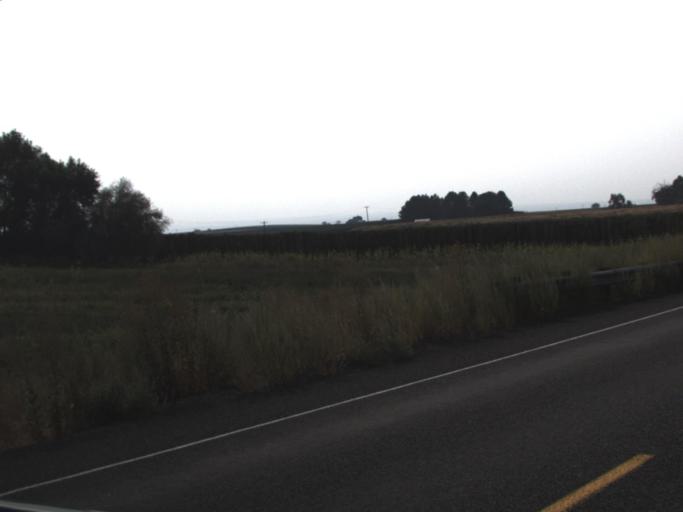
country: US
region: Washington
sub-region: Yakima County
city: Mabton
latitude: 46.2161
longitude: -120.0178
